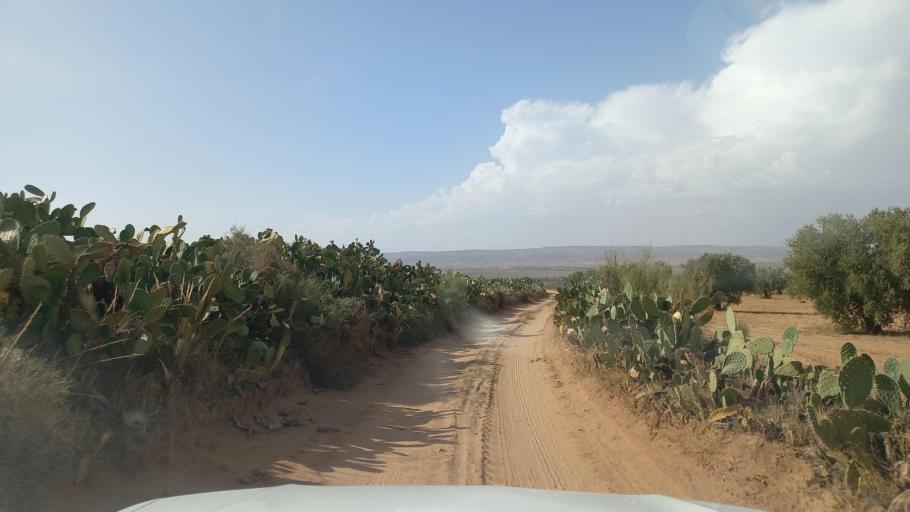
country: TN
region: Al Qasrayn
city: Kasserine
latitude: 35.2070
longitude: 8.9682
